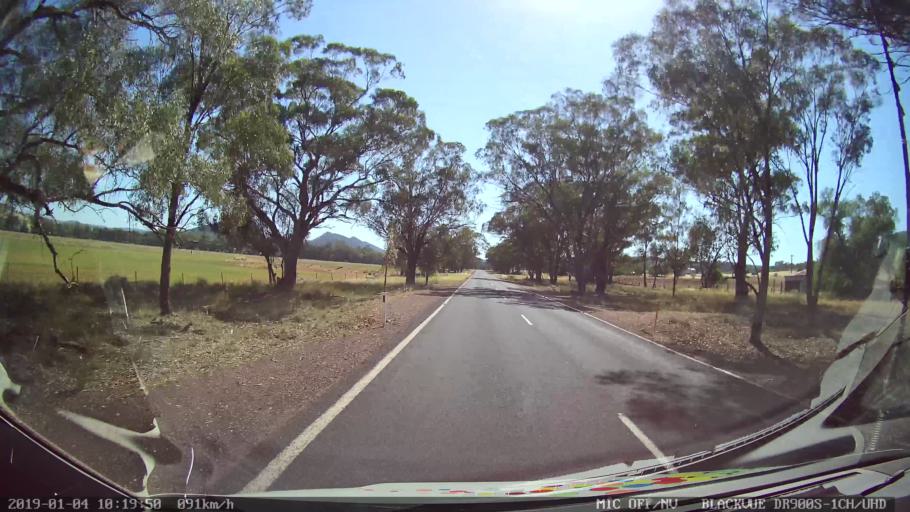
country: AU
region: New South Wales
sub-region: Cabonne
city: Canowindra
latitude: -33.3748
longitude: 148.4867
